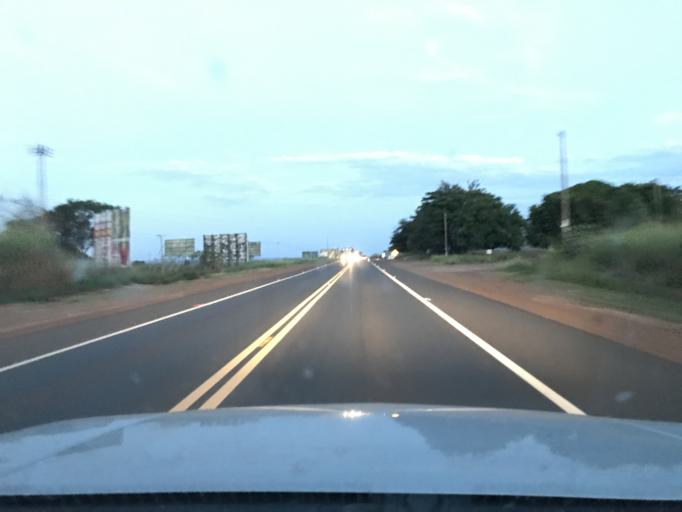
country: PY
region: Canindeyu
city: Salto del Guaira
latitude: -24.0233
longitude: -54.2914
